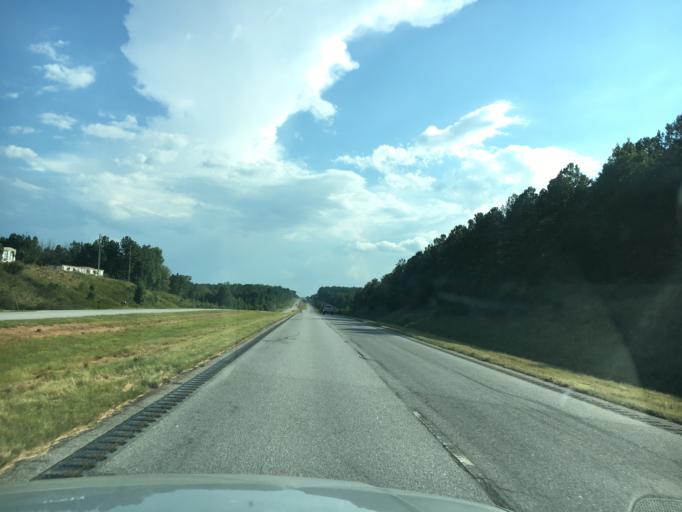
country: US
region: South Carolina
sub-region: Greenwood County
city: Ninety Six
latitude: 34.3352
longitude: -81.9835
